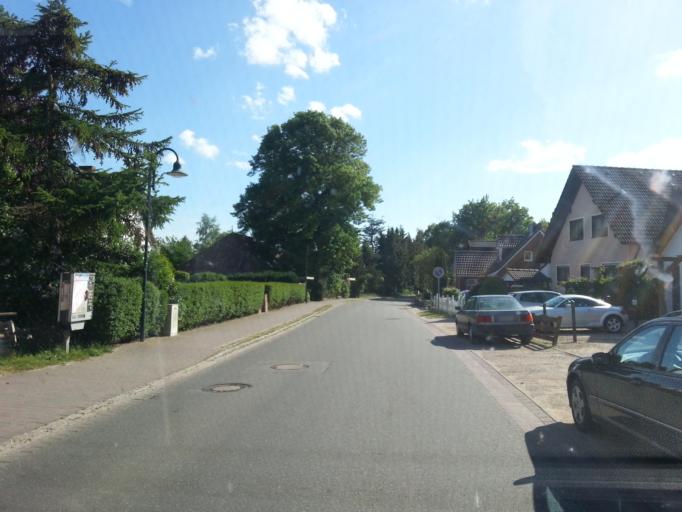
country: DE
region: Schleswig-Holstein
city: Scharbeutz
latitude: 53.9987
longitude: 10.7207
